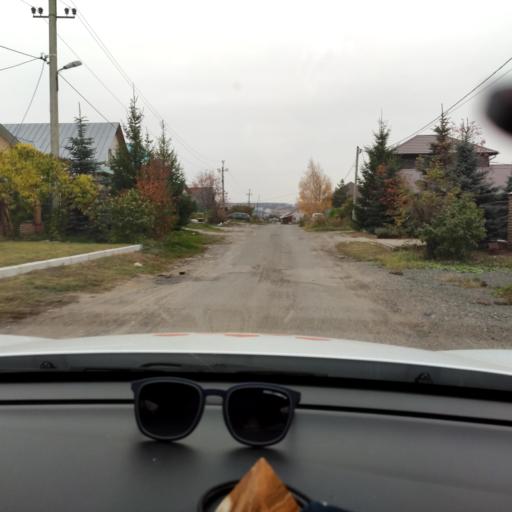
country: RU
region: Tatarstan
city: Vysokaya Gora
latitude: 55.8111
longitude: 49.2504
